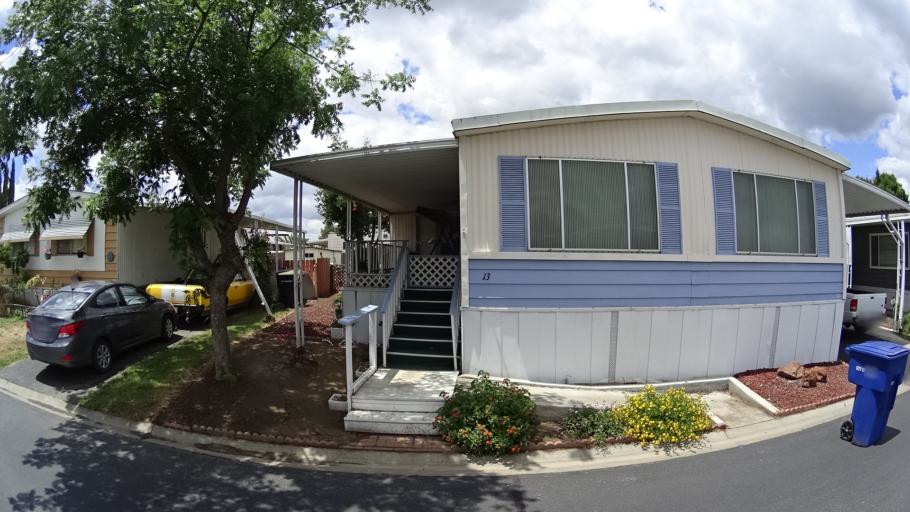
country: US
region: California
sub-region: Kings County
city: Hanford
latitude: 36.3447
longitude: -119.6332
